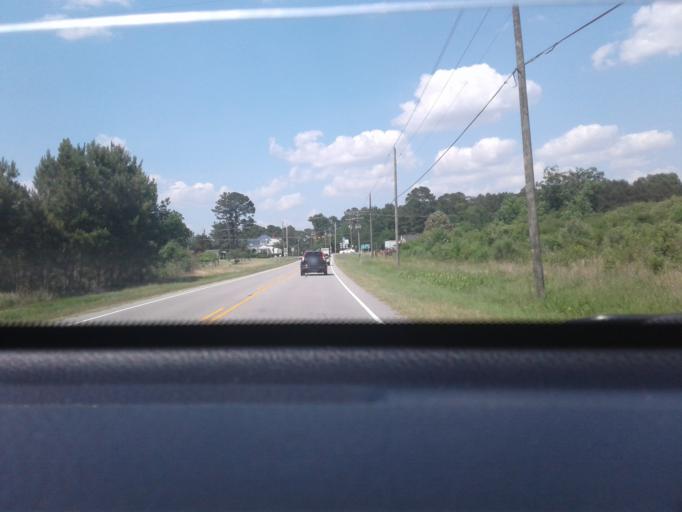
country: US
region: North Carolina
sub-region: Harnett County
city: Erwin
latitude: 35.2147
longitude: -78.6791
